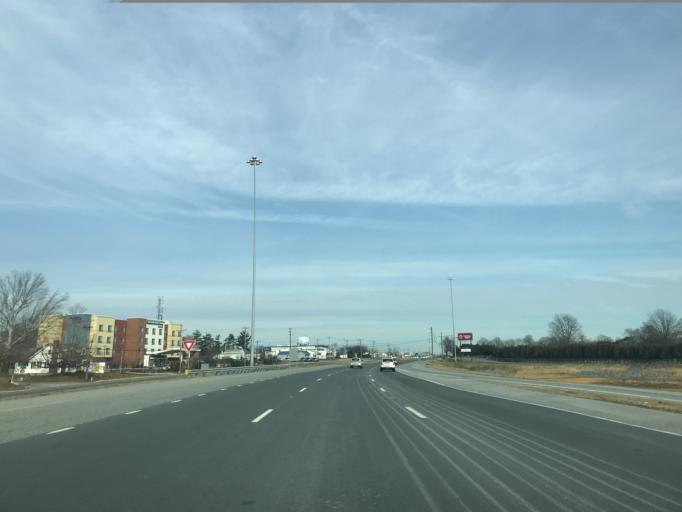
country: US
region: Delaware
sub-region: New Castle County
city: Wilmington Manor
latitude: 39.6995
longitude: -75.5724
